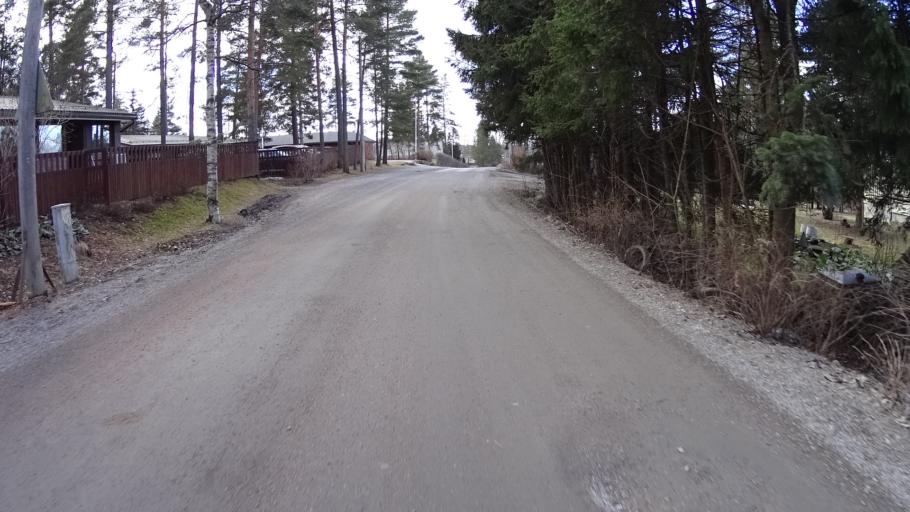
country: FI
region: Uusimaa
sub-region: Helsinki
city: Kauniainen
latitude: 60.2365
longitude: 24.7483
